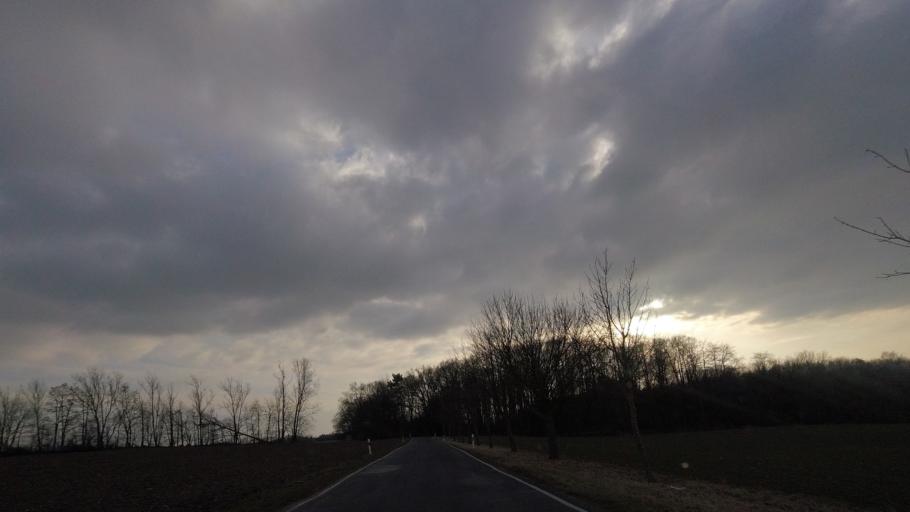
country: DE
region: Brandenburg
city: Belzig
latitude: 52.1512
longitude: 12.5227
